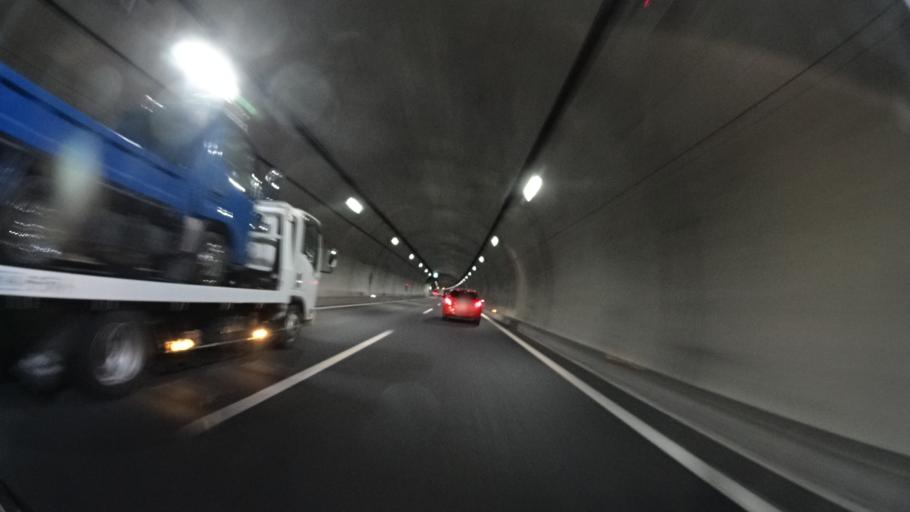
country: JP
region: Ibaraki
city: Kasama
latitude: 36.3405
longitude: 140.2371
